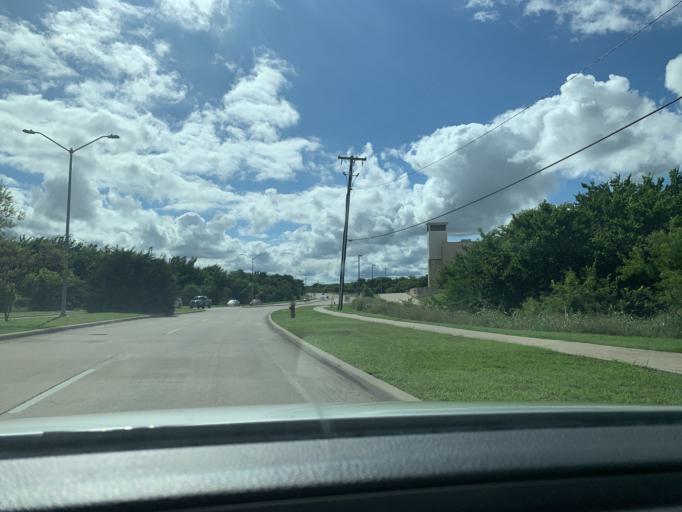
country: US
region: Texas
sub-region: Dallas County
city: Grand Prairie
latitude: 32.6673
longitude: -97.0208
